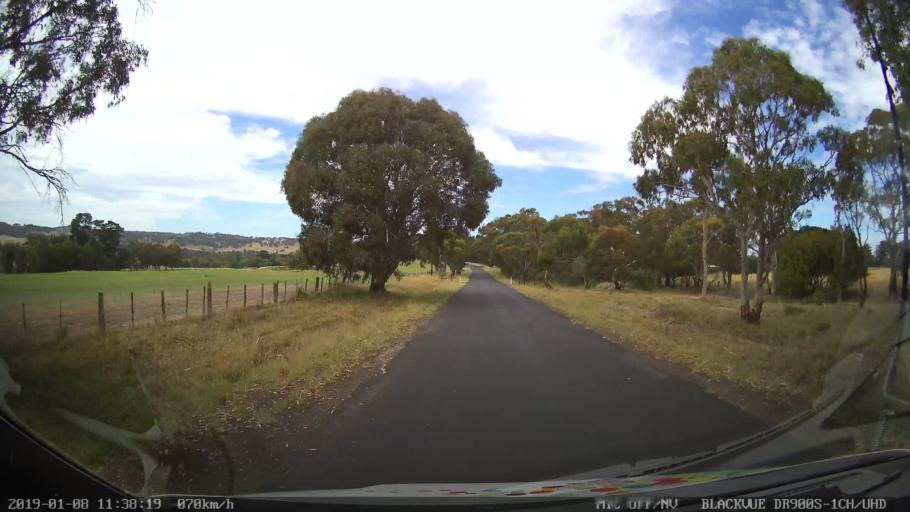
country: AU
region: New South Wales
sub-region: Guyra
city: Guyra
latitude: -30.3596
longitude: 151.5553
